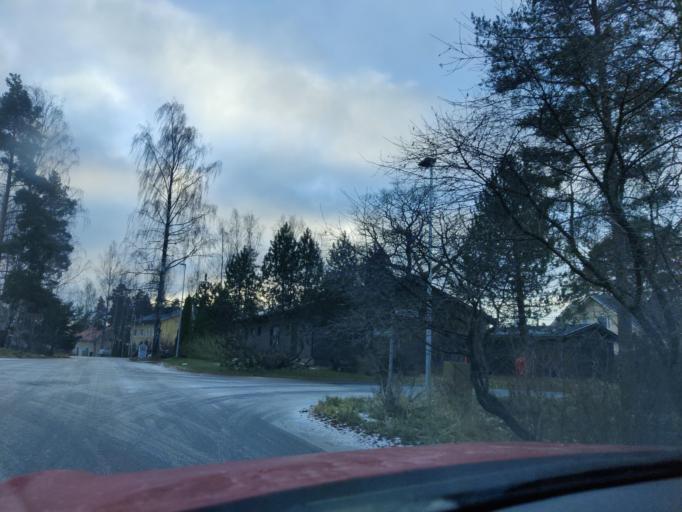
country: FI
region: Pirkanmaa
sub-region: Tampere
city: Nokia
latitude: 61.4642
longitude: 23.4772
